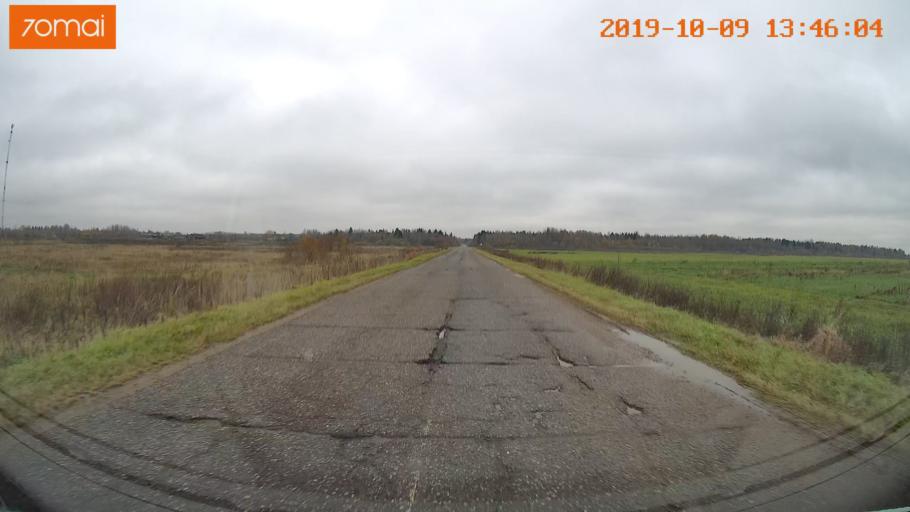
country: RU
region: Kostroma
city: Buy
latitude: 58.3802
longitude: 41.2150
